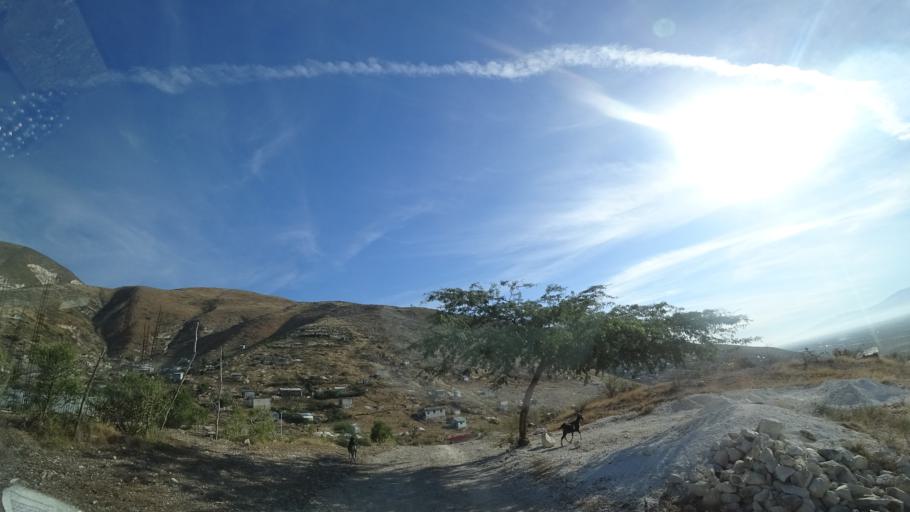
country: HT
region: Ouest
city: Croix des Bouquets
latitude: 18.6695
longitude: -72.2258
